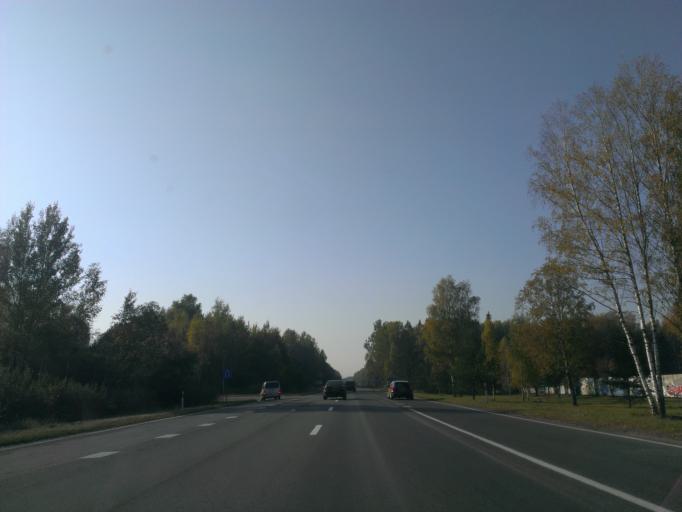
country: LV
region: Incukalns
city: Vangazi
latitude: 57.0877
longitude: 24.5460
